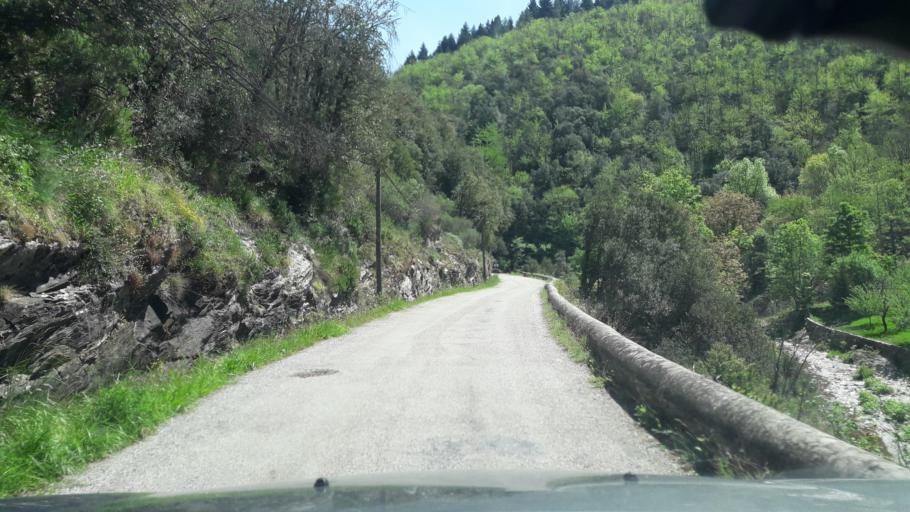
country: FR
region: Languedoc-Roussillon
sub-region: Departement du Gard
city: Valleraugue
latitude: 44.1176
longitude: 3.7126
